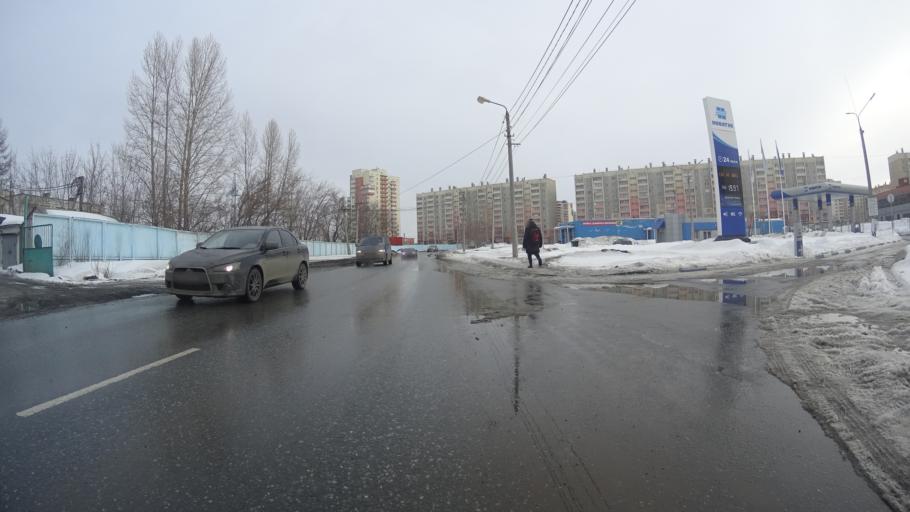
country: RU
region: Chelyabinsk
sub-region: Gorod Chelyabinsk
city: Chelyabinsk
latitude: 55.1685
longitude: 61.2983
